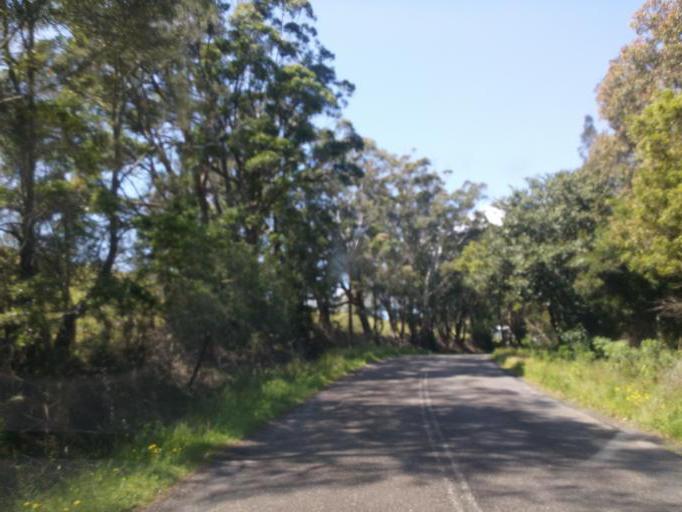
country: AU
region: New South Wales
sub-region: Great Lakes
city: Bulahdelah
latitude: -32.3919
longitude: 152.4360
